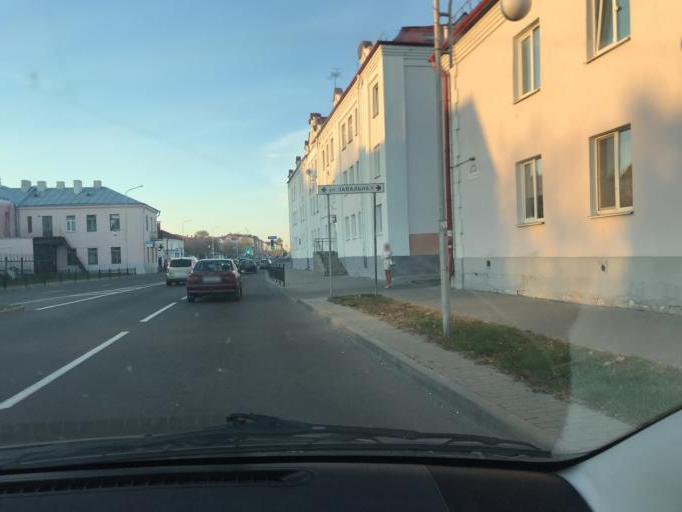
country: BY
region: Brest
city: Pinsk
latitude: 52.1145
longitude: 26.1036
